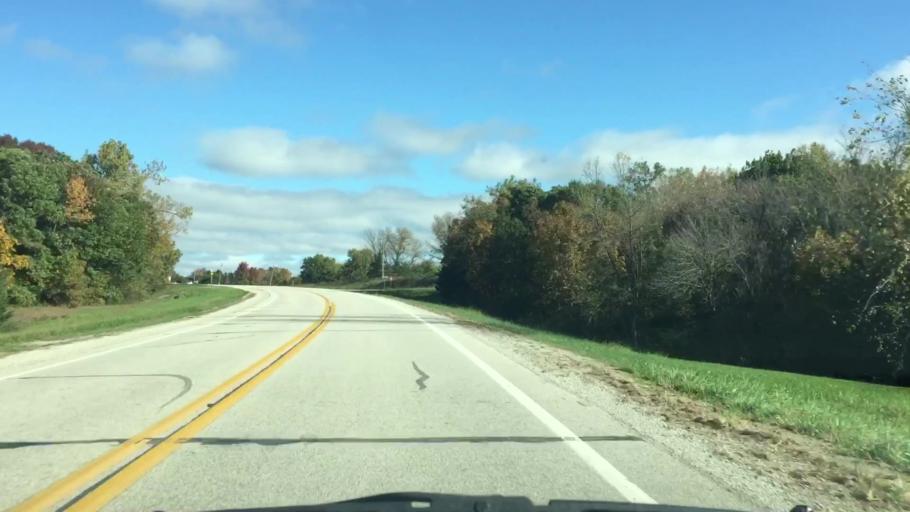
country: US
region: Iowa
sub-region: Decatur County
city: Leon
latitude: 40.6883
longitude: -93.7757
